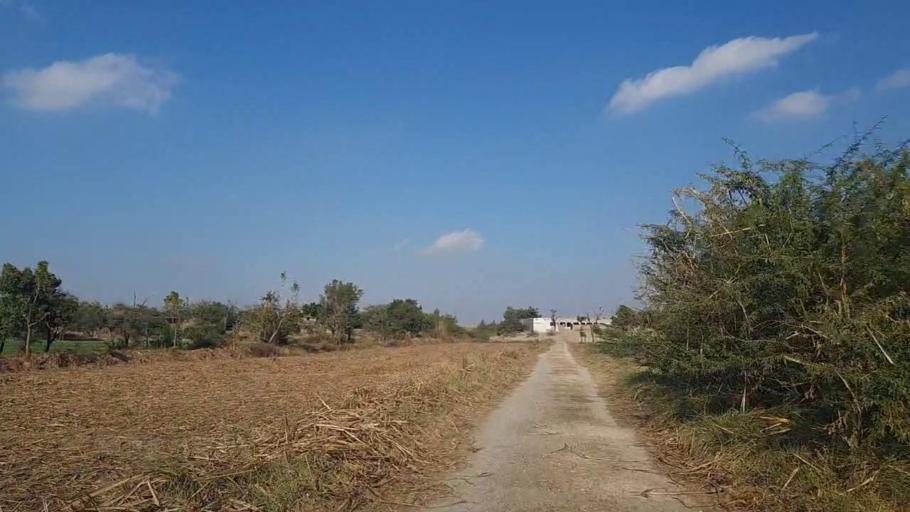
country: PK
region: Sindh
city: Tando Mittha Khan
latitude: 26.0065
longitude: 69.2619
